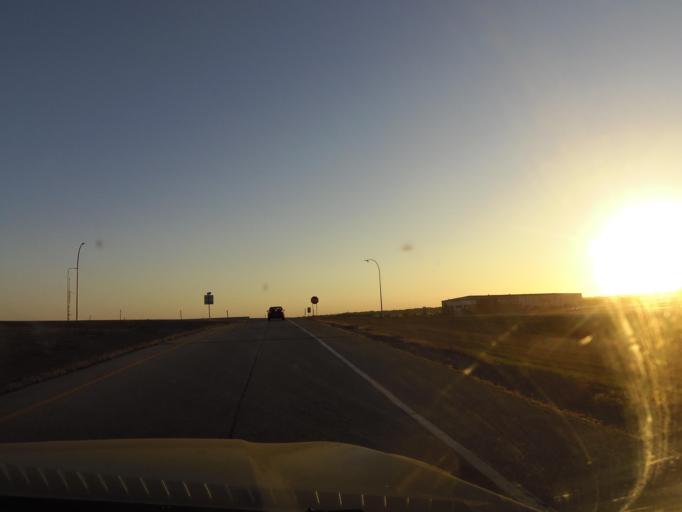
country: US
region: North Dakota
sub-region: Traill County
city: Hillsboro
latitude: 47.4039
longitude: -97.0760
